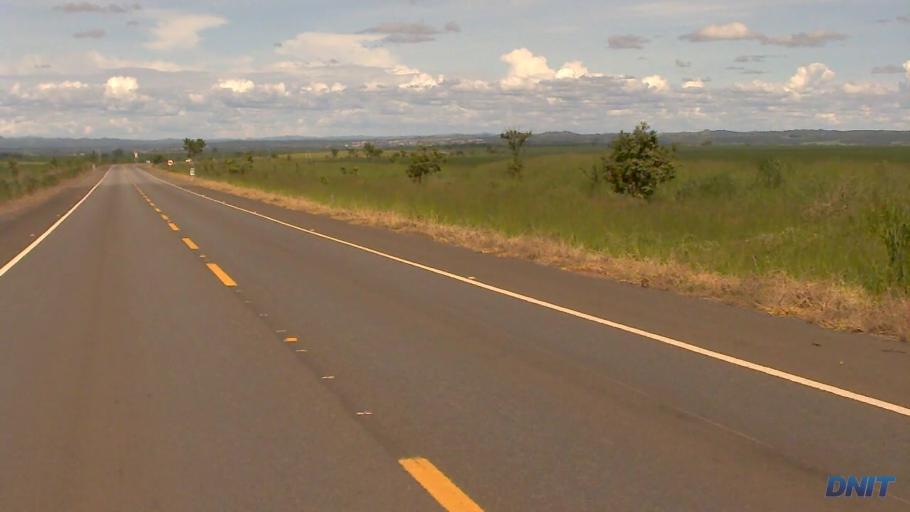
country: BR
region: Goias
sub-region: Padre Bernardo
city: Padre Bernardo
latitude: -15.1740
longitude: -48.3965
